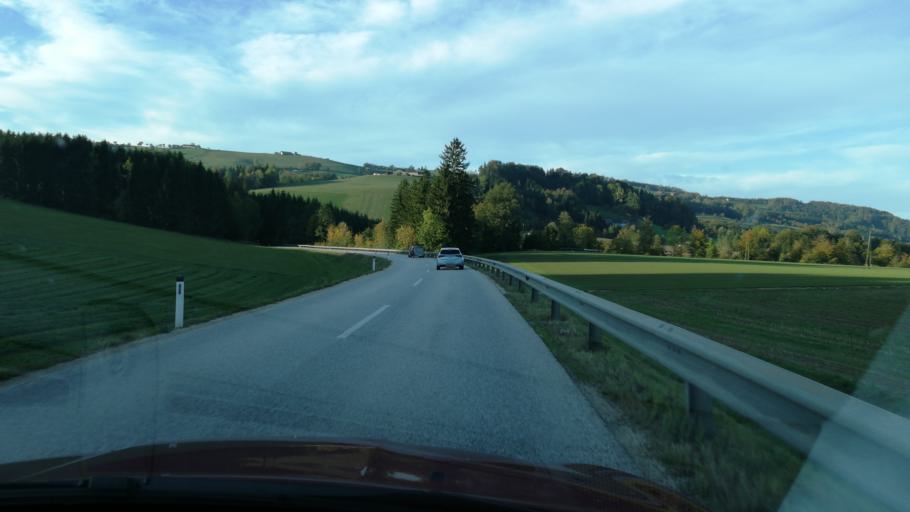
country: AT
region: Upper Austria
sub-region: Politischer Bezirk Steyr-Land
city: Ternberg
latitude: 47.9685
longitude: 14.3443
